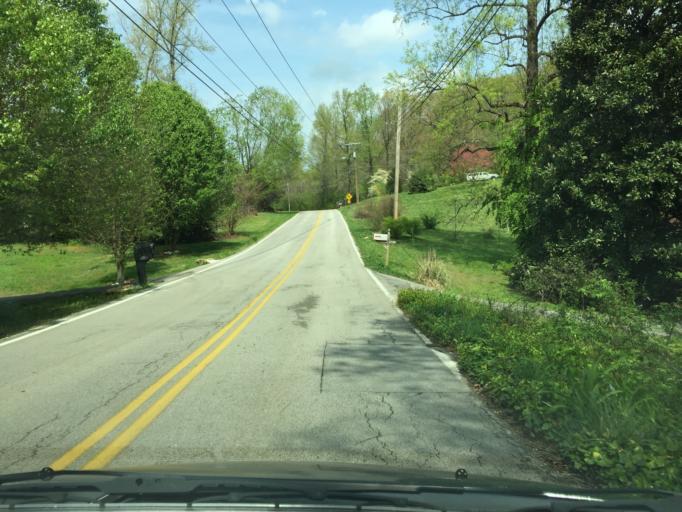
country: US
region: Tennessee
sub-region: Hamilton County
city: Walden
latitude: 35.1582
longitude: -85.2787
